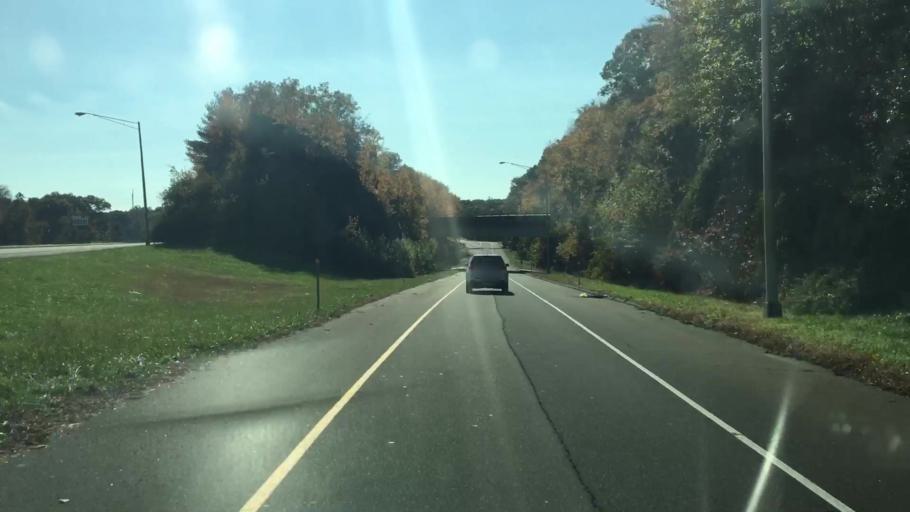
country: US
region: Connecticut
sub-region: Fairfield County
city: Trumbull
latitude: 41.2407
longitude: -73.1906
